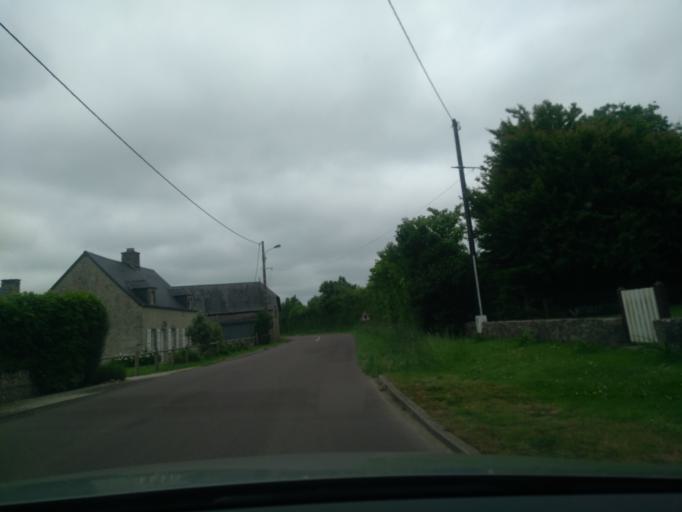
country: FR
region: Lower Normandy
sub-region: Departement de la Manche
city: Sainte-Mere-Eglise
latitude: 49.4290
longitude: -1.3038
